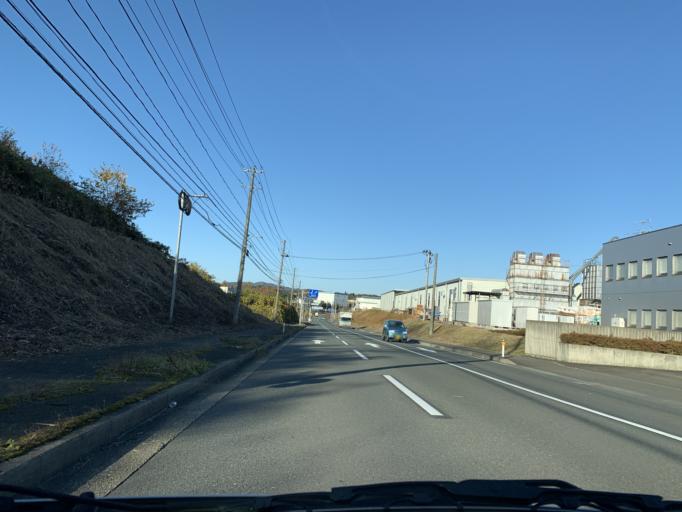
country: JP
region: Iwate
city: Mizusawa
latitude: 39.2054
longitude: 141.1782
